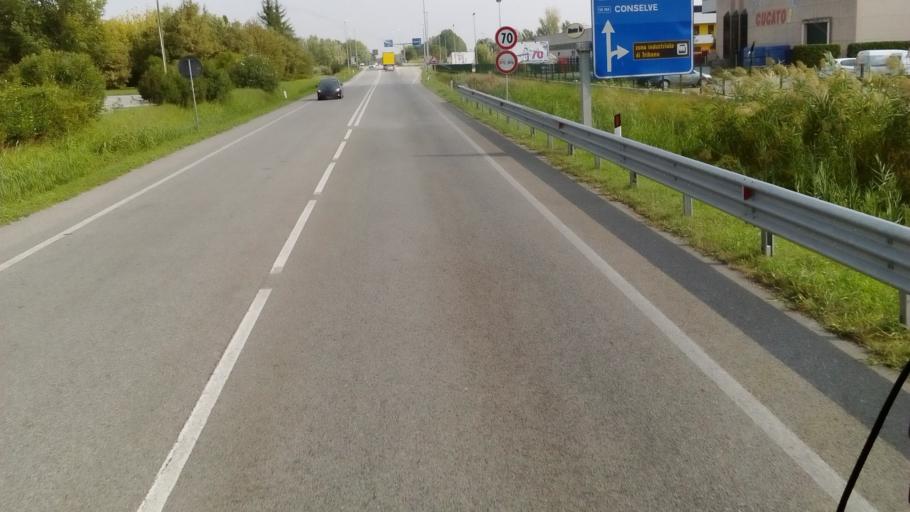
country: IT
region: Veneto
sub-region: Provincia di Padova
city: Tribano
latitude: 45.2151
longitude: 11.8416
